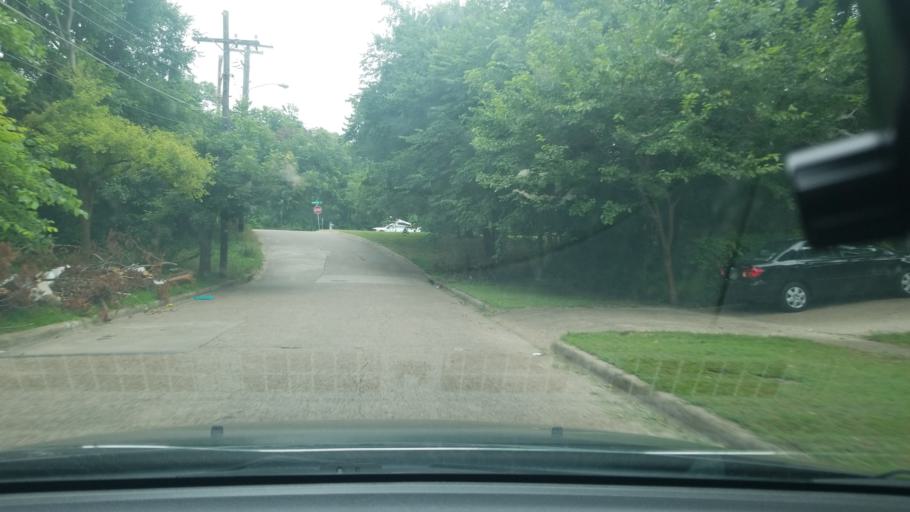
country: US
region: Texas
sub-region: Dallas County
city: Balch Springs
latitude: 32.7642
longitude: -96.6938
